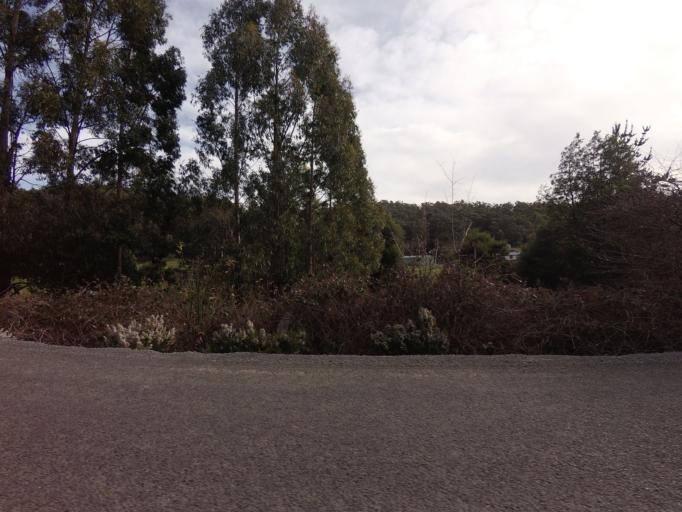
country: AU
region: Tasmania
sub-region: Kingborough
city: Margate
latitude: -42.9887
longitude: 147.1906
